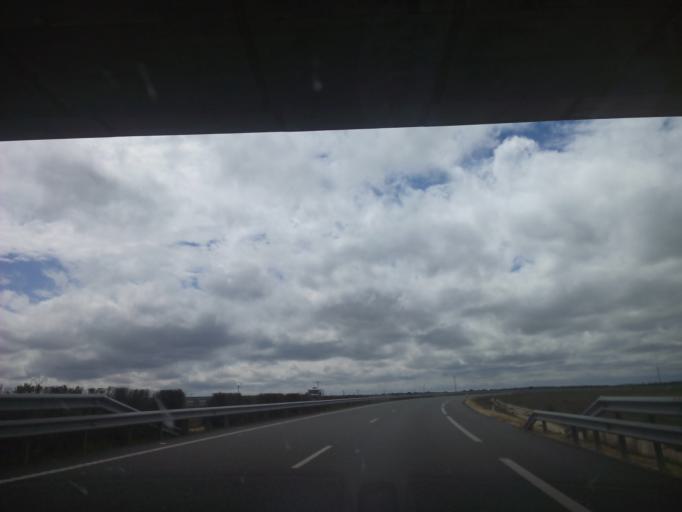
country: ES
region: Castille and Leon
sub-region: Provincia de Salamanca
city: Pelabravo
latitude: 40.9298
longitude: -5.5750
